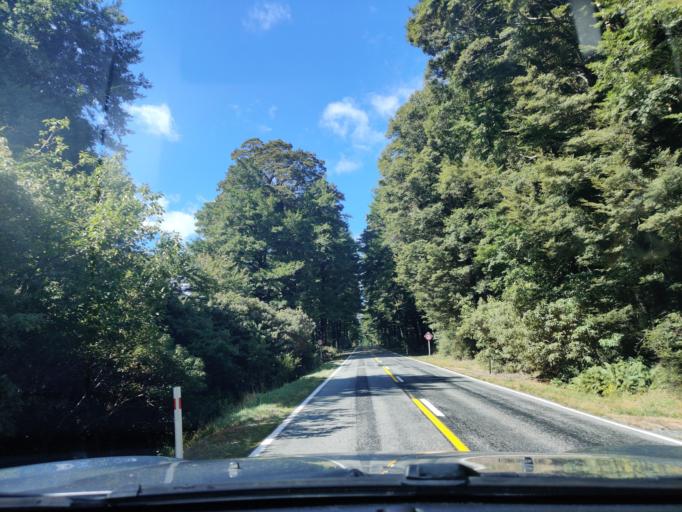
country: NZ
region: Canterbury
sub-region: Hurunui District
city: Amberley
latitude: -42.3799
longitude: 172.3274
